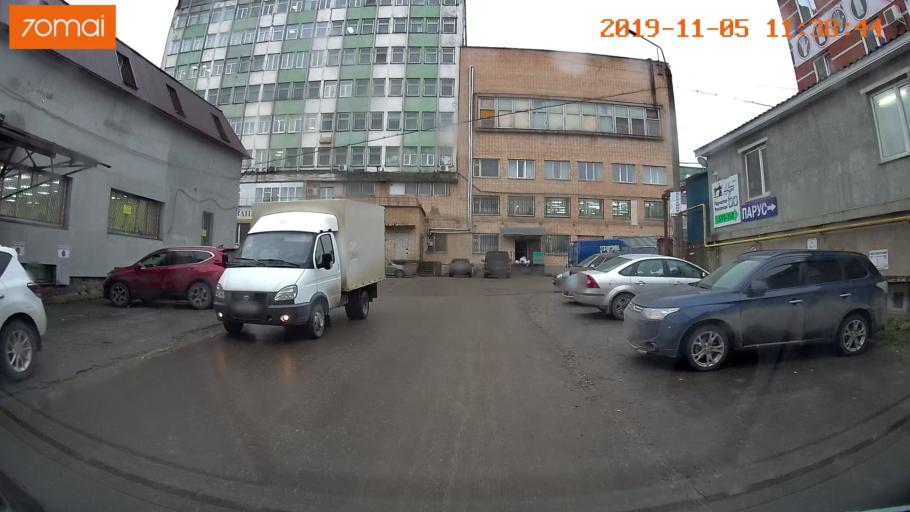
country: RU
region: Ivanovo
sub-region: Gorod Ivanovo
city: Ivanovo
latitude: 57.0098
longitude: 40.9583
